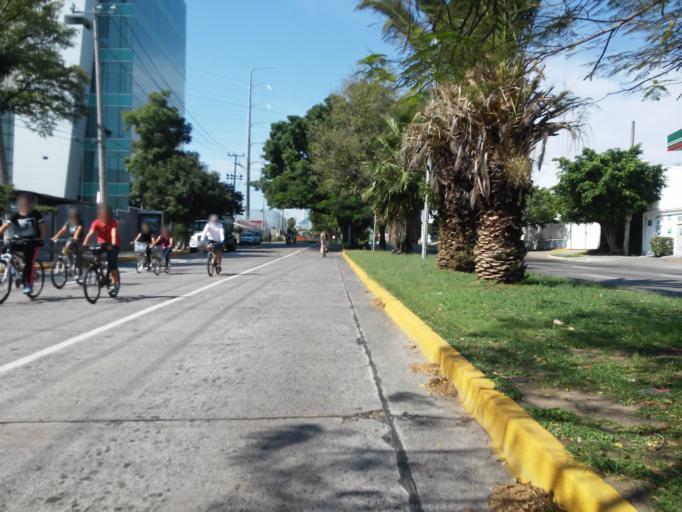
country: MX
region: Jalisco
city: Guadalajara
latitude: 20.6667
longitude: -103.3768
